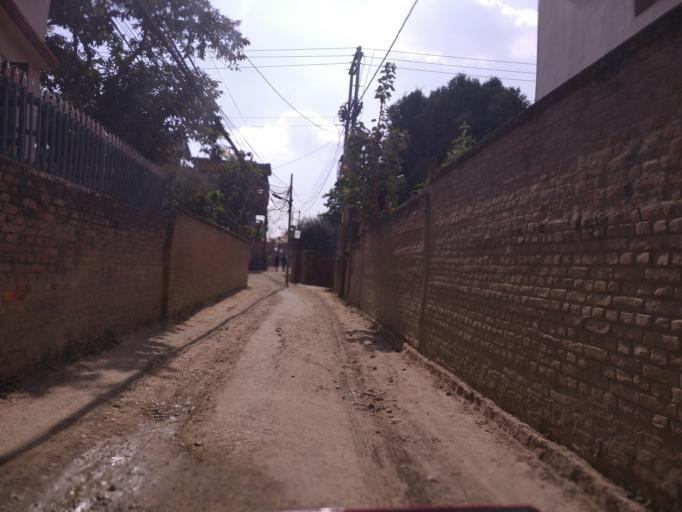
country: NP
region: Central Region
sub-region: Bagmati Zone
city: Patan
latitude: 27.6657
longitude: 85.3163
